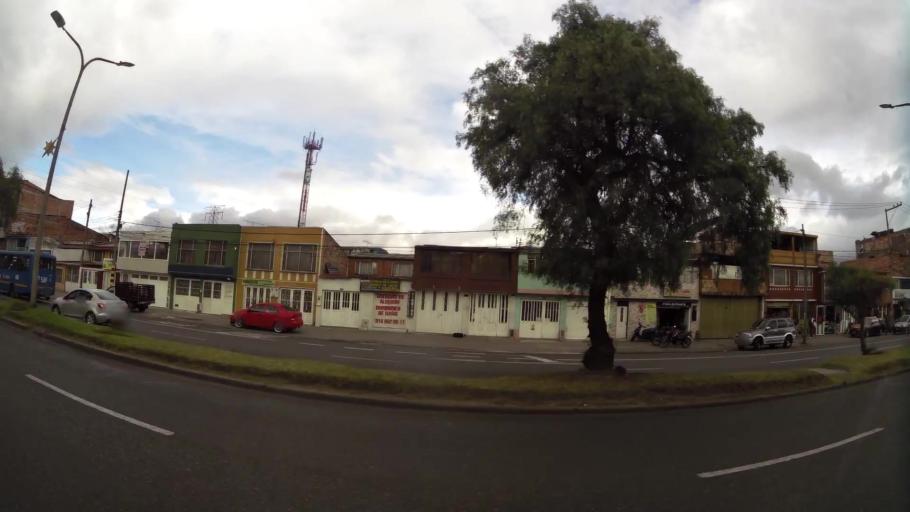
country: CO
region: Bogota D.C.
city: Bogota
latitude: 4.6128
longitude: -74.1158
